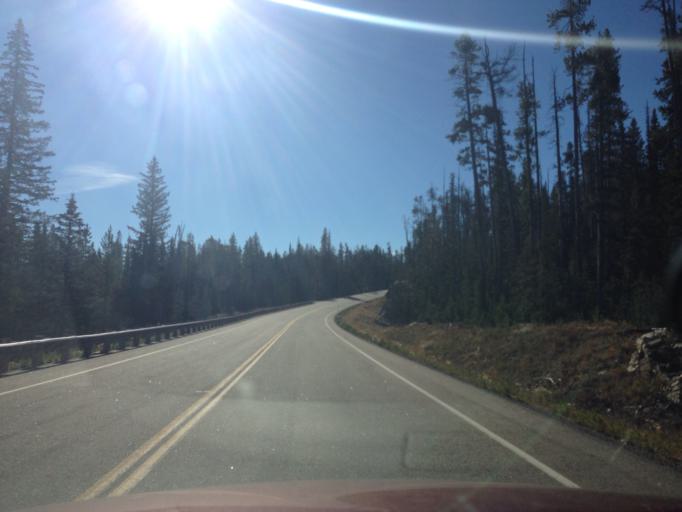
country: US
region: Montana
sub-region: Carbon County
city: Red Lodge
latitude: 45.0180
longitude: -109.8722
